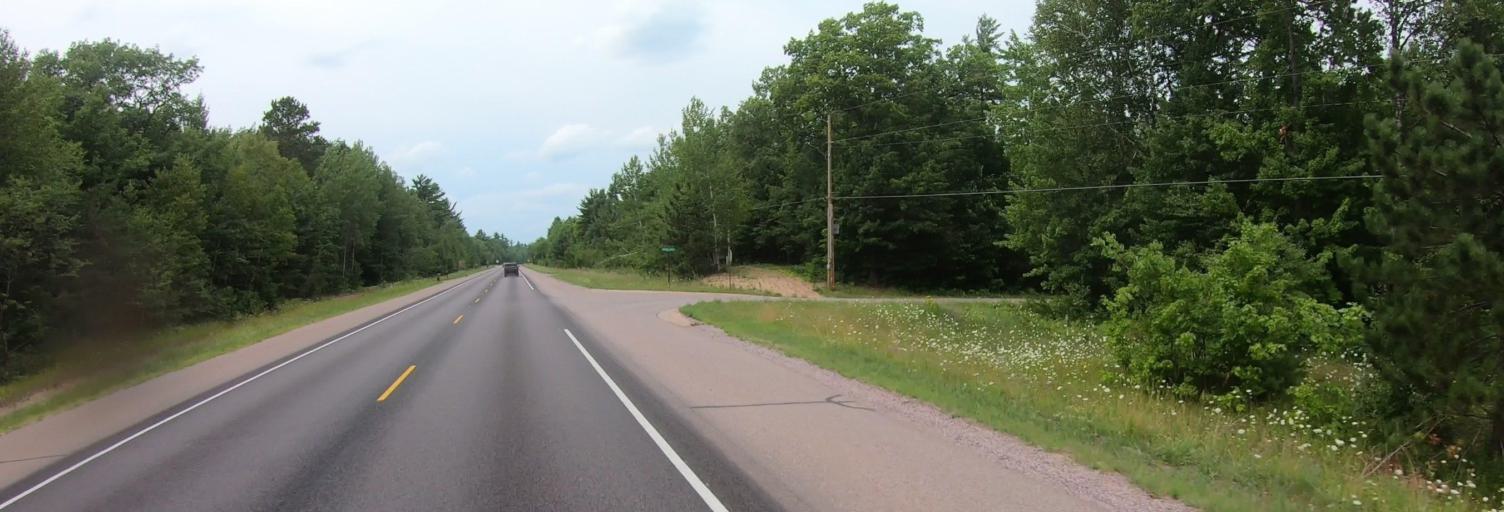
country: US
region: Michigan
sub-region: Marquette County
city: Harvey
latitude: 46.4672
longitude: -87.4331
